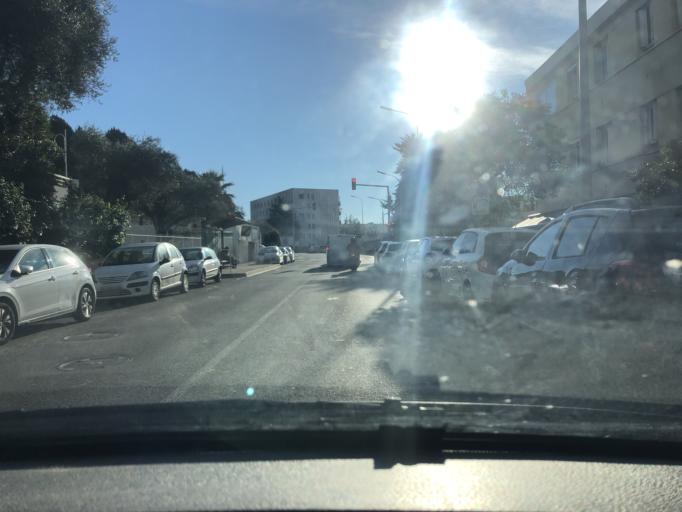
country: FR
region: Provence-Alpes-Cote d'Azur
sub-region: Departement des Alpes-Maritimes
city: Saint-Laurent-du-Var
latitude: 43.6748
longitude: 7.2114
